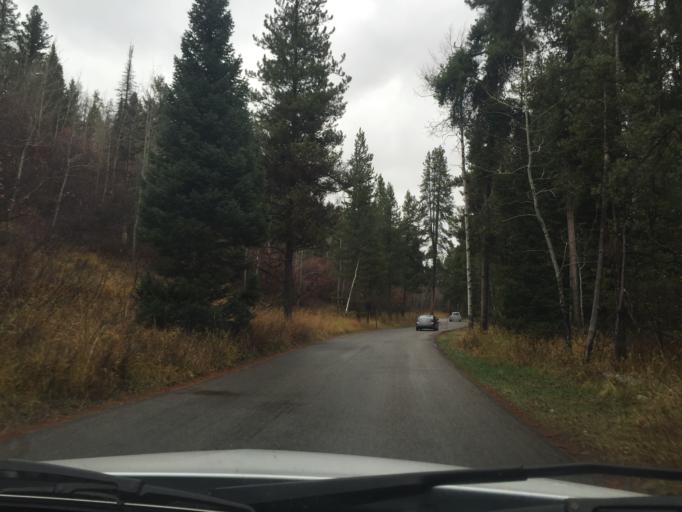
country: US
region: Wyoming
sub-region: Teton County
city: Moose Wilson Road
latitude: 43.6338
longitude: -110.7711
